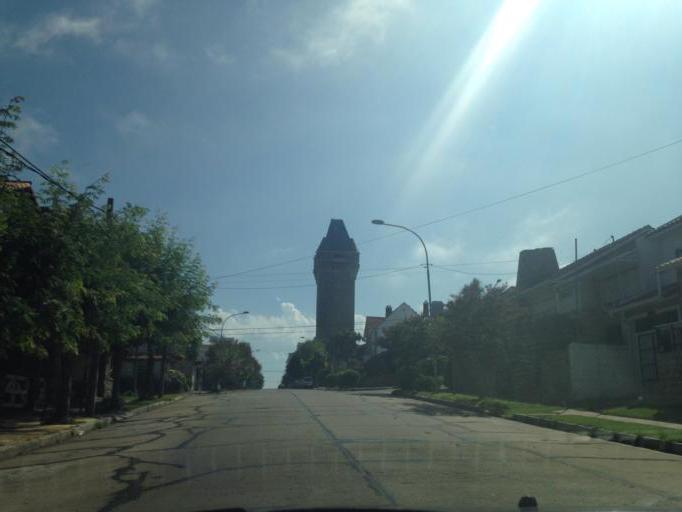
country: AR
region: Buenos Aires
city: Mar del Plata
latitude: -38.0144
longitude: -57.5364
